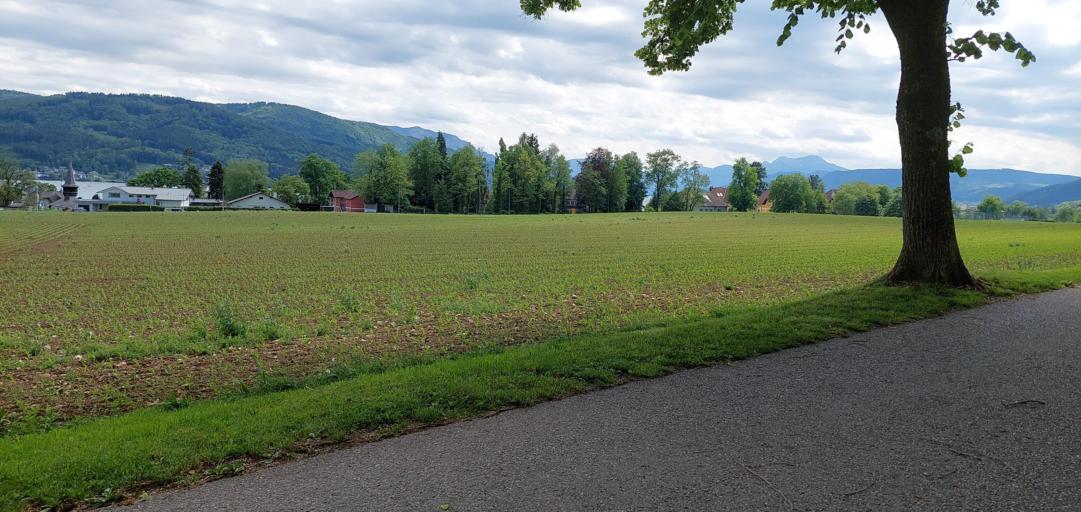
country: AT
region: Upper Austria
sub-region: Politischer Bezirk Vocklabruck
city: Seewalchen
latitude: 47.9535
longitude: 13.5845
